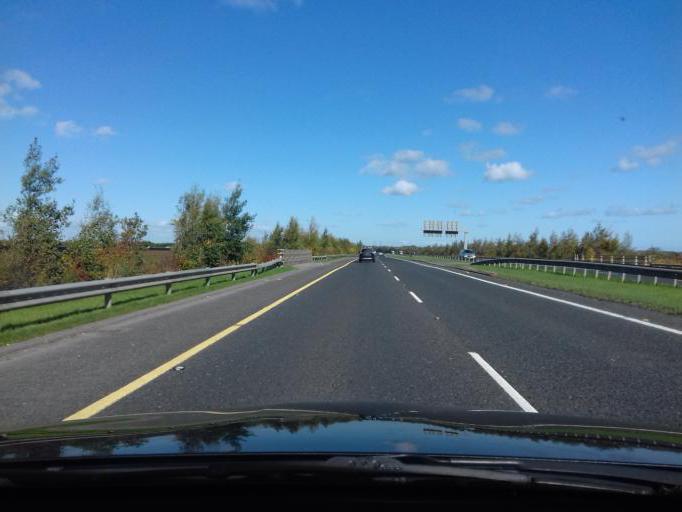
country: IE
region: Leinster
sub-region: Fingal County
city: Blanchardstown
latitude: 53.4464
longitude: -6.3556
